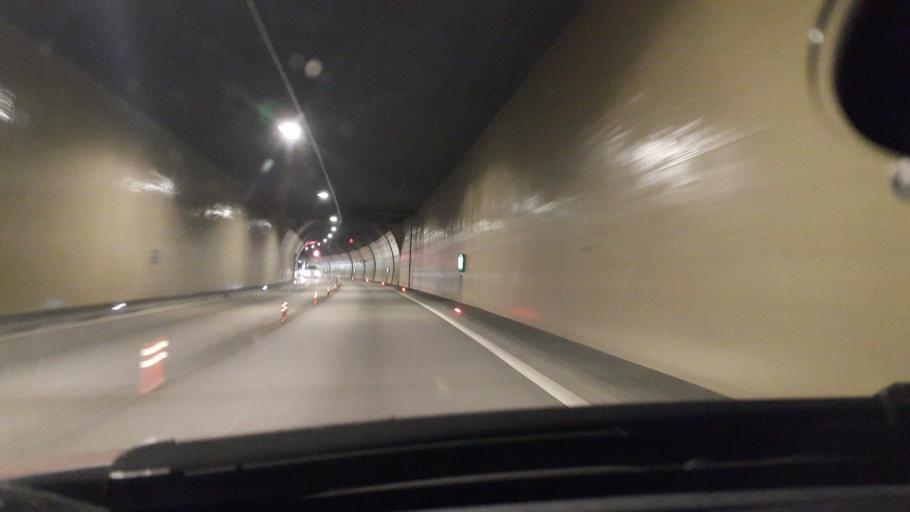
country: AT
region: Carinthia
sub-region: Klagenfurt am Woerthersee
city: Klagenfurt am Woerthersee
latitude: 46.6498
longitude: 14.3241
